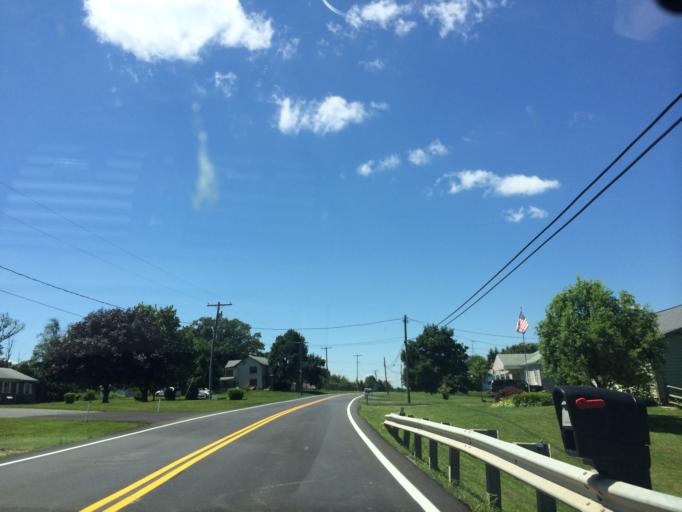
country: US
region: Maryland
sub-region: Frederick County
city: Woodsboro
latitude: 39.5174
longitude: -77.2897
